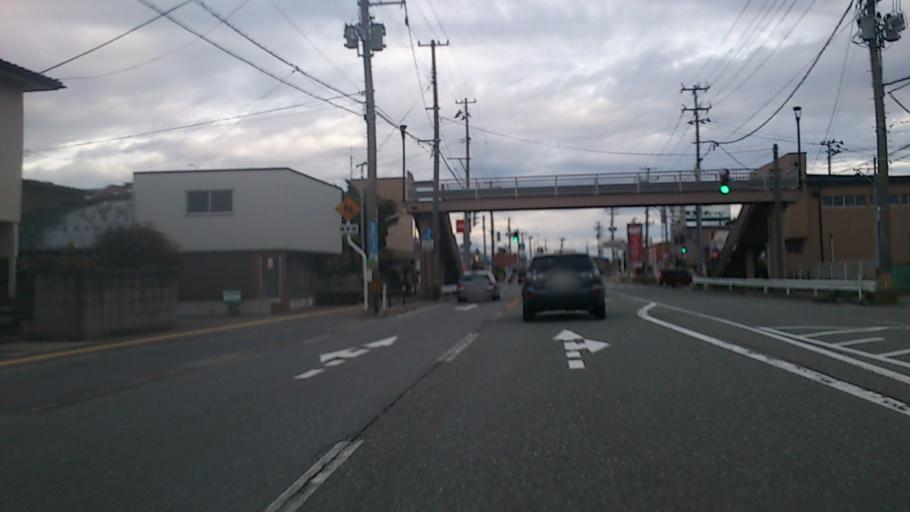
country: JP
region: Akita
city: Akita Shi
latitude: 39.7464
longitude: 140.0841
